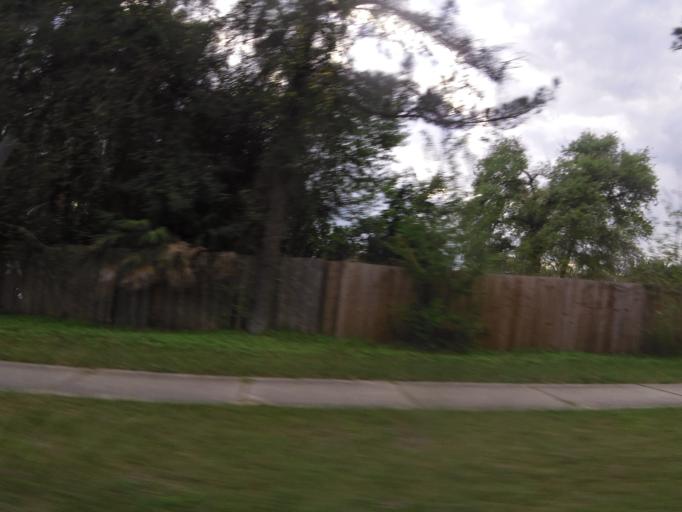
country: US
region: Florida
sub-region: Saint Johns County
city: Fruit Cove
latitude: 30.2157
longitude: -81.5861
